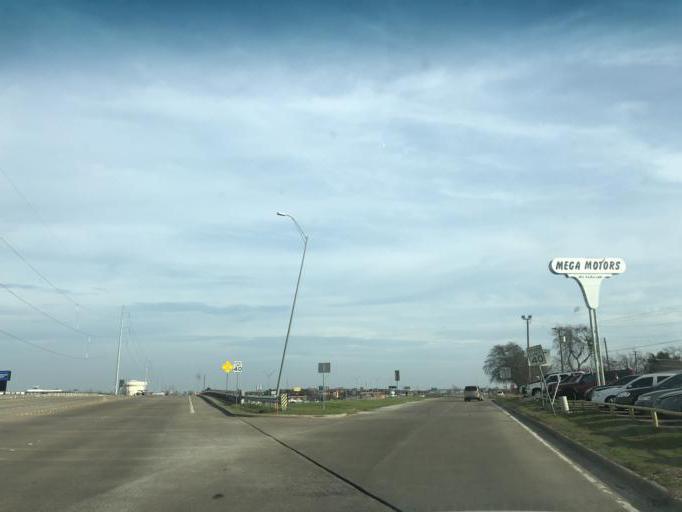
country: US
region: Texas
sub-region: Dallas County
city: Duncanville
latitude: 32.6619
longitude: -96.8972
